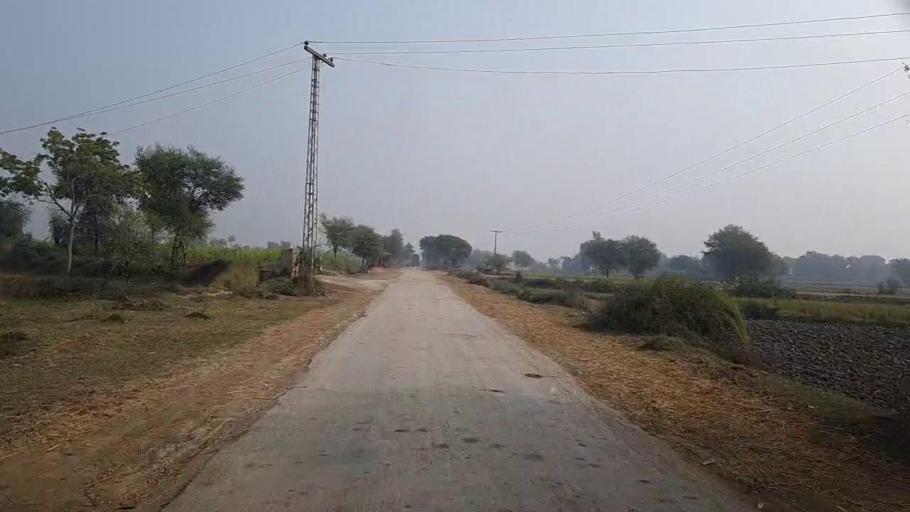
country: PK
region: Sindh
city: Dadu
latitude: 26.8368
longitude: 67.7750
